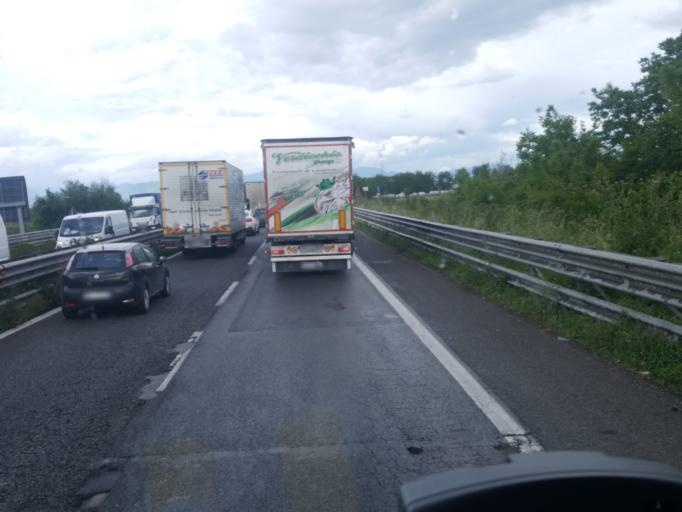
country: IT
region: Campania
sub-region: Provincia di Napoli
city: Pascarola
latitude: 40.9734
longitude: 14.2946
